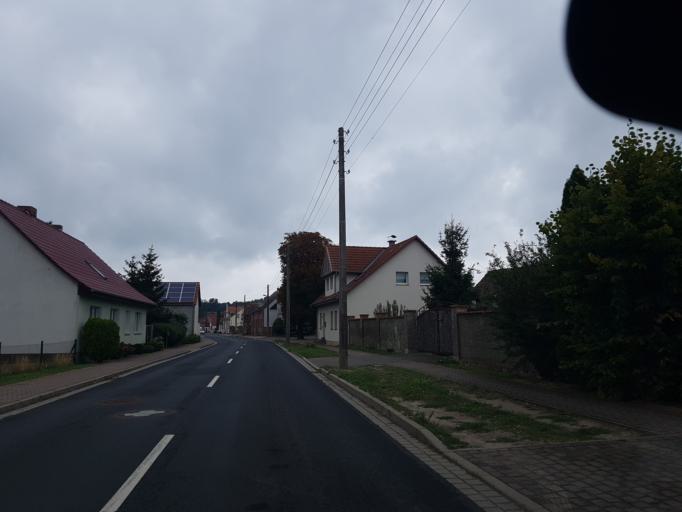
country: DE
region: Saxony-Anhalt
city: Tucheim
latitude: 52.3140
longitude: 12.1195
